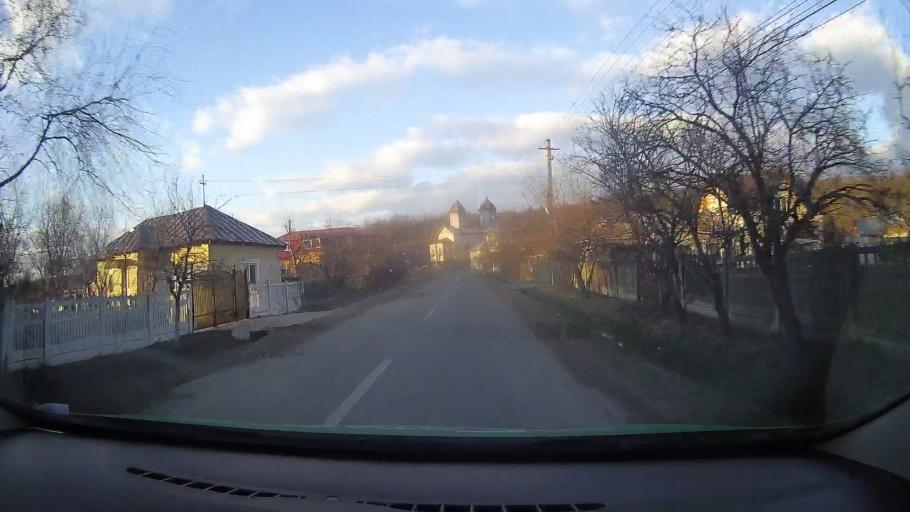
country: RO
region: Dambovita
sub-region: Comuna Gura Ocnitei
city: Adanca
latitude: 44.9178
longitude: 25.6162
